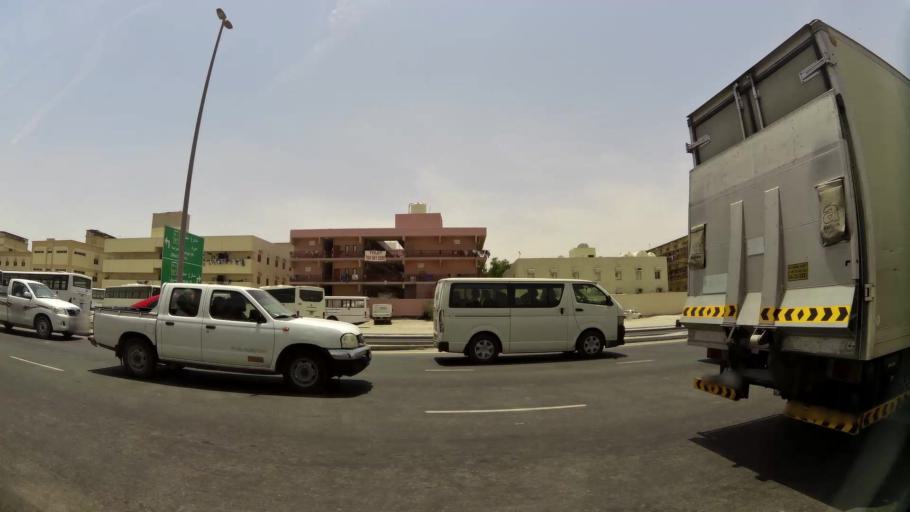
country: AE
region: Ash Shariqah
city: Sharjah
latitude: 25.2731
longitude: 55.4316
